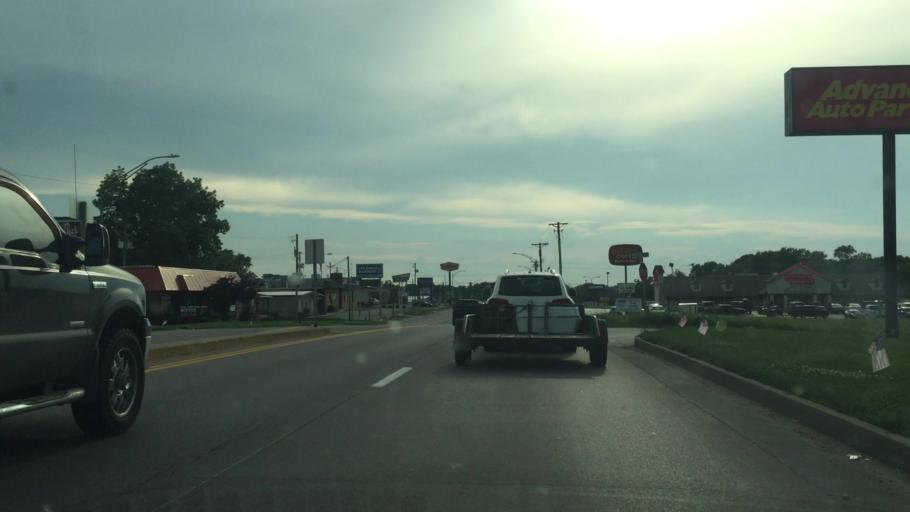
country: US
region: Missouri
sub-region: Pettis County
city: Sedalia
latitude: 38.7052
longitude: -93.2515
